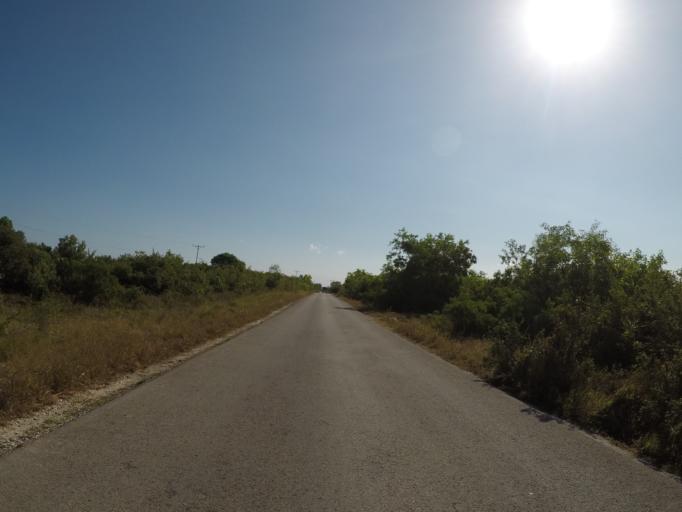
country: TZ
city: Kiwengwa
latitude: -6.1425
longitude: 39.5092
